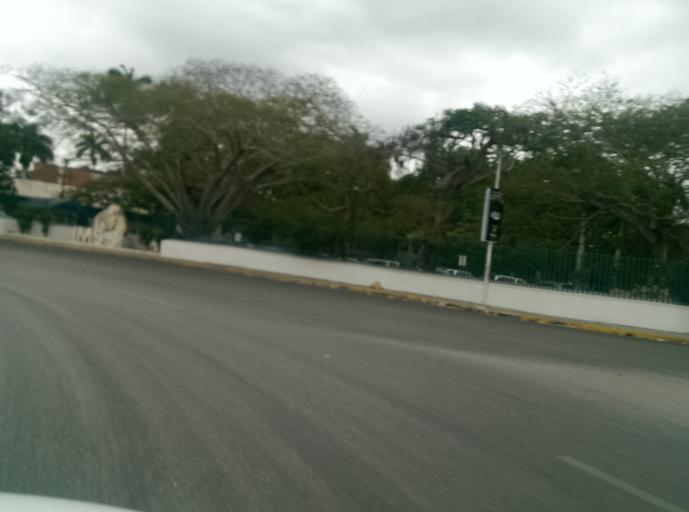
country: MX
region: Yucatan
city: Merida
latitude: 20.9889
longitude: -89.6390
